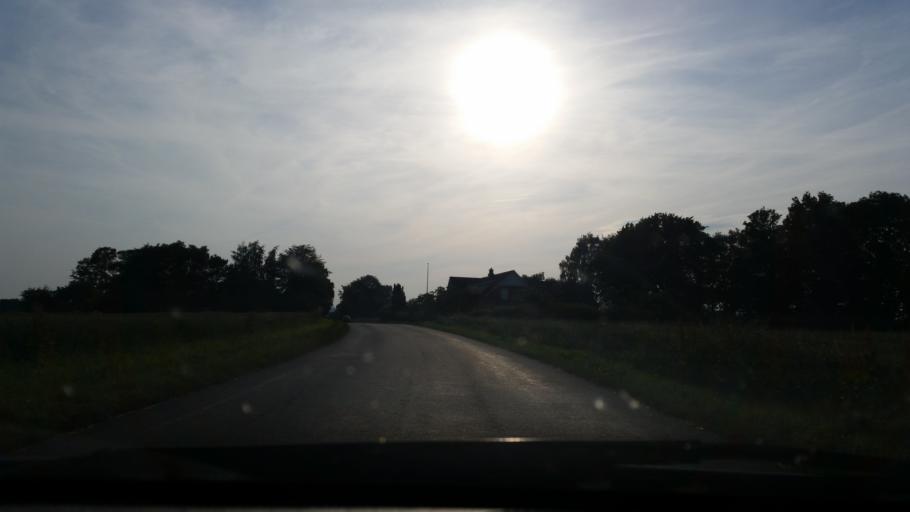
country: DK
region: Central Jutland
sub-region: Odder Kommune
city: Odder
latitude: 55.8906
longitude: 10.1596
